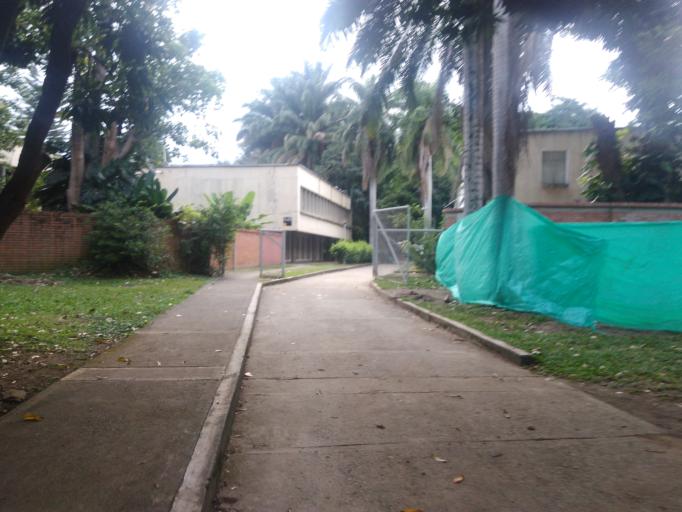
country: CO
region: Valle del Cauca
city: Cali
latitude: 3.3752
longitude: -76.5317
